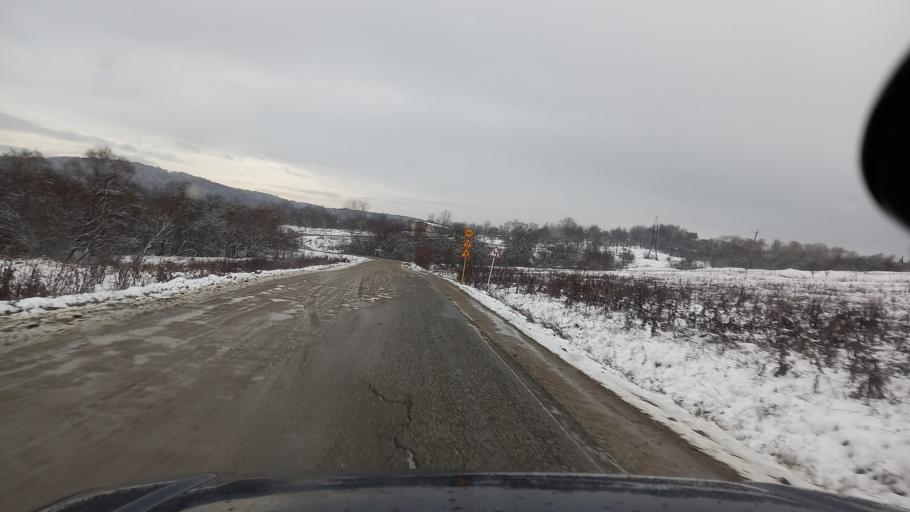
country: RU
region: Adygeya
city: Abadzekhskaya
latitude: 44.3590
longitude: 40.4002
